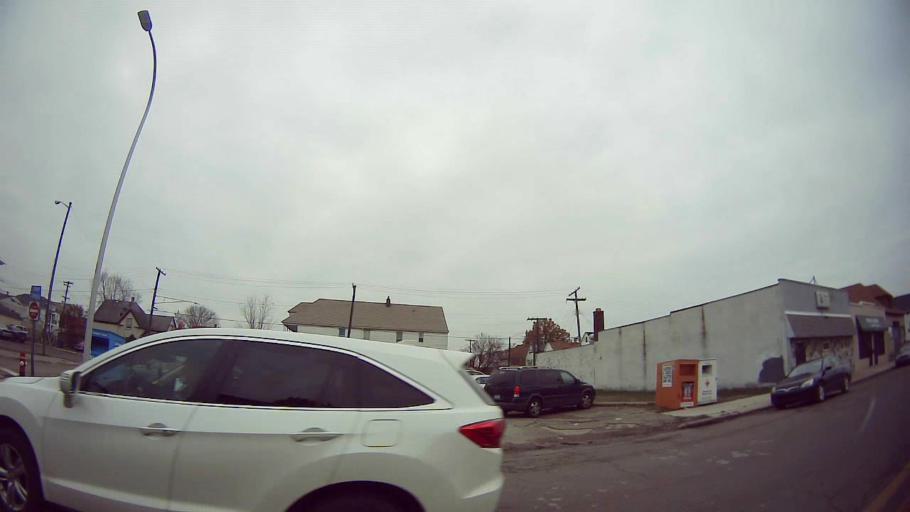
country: US
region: Michigan
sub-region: Wayne County
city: Hamtramck
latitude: 42.3972
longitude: -83.0491
